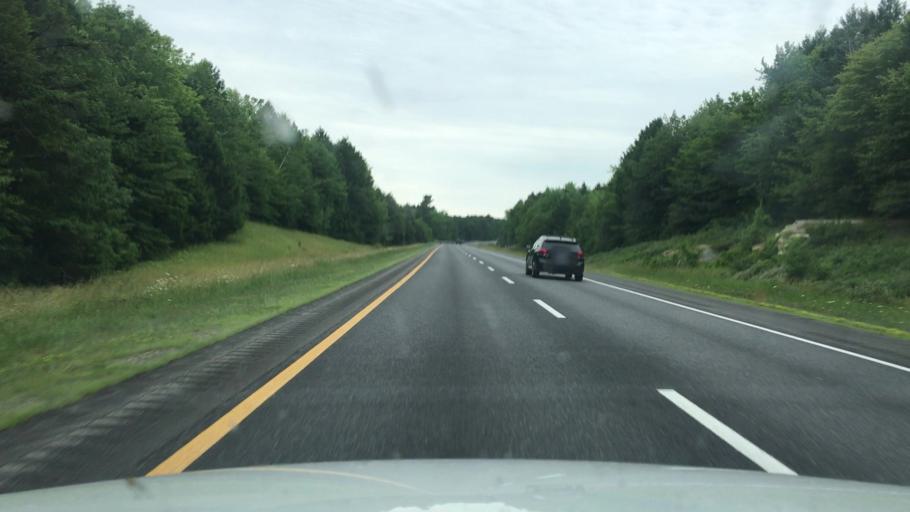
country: US
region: Maine
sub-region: Sagadahoc County
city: Richmond
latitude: 44.0489
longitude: -69.8942
